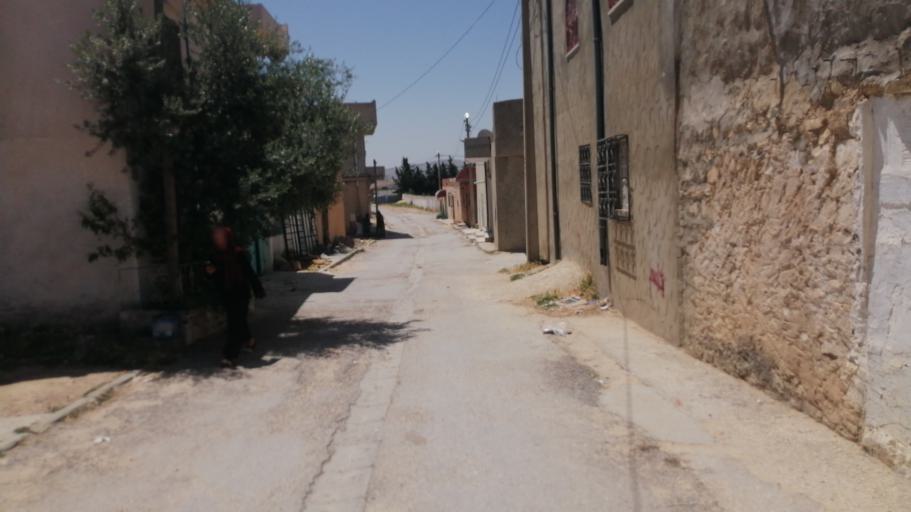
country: TN
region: Silyanah
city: Maktar
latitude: 35.8499
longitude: 9.2041
